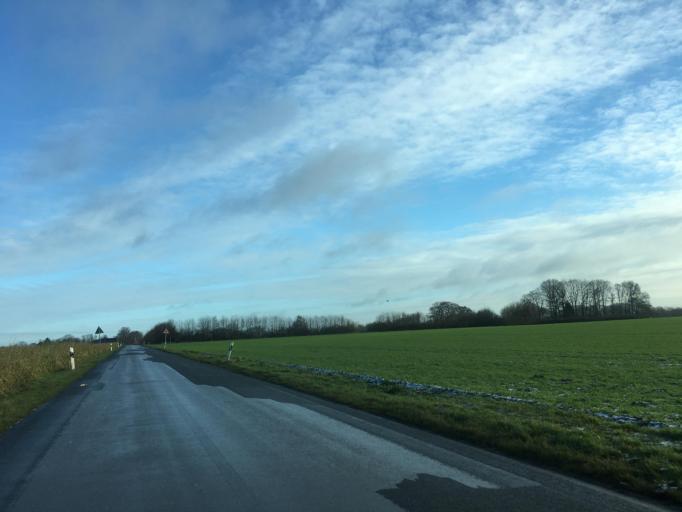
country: DE
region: North Rhine-Westphalia
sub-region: Regierungsbezirk Munster
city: Dulmen
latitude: 51.8102
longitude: 7.3077
